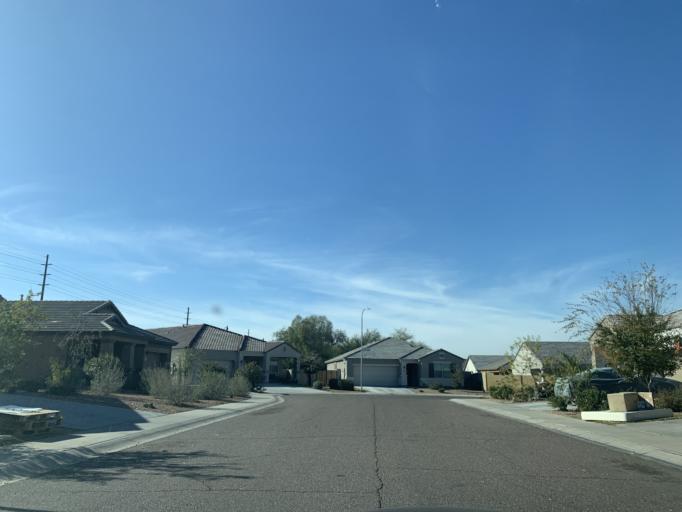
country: US
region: Arizona
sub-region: Maricopa County
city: Laveen
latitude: 33.3927
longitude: -112.1198
